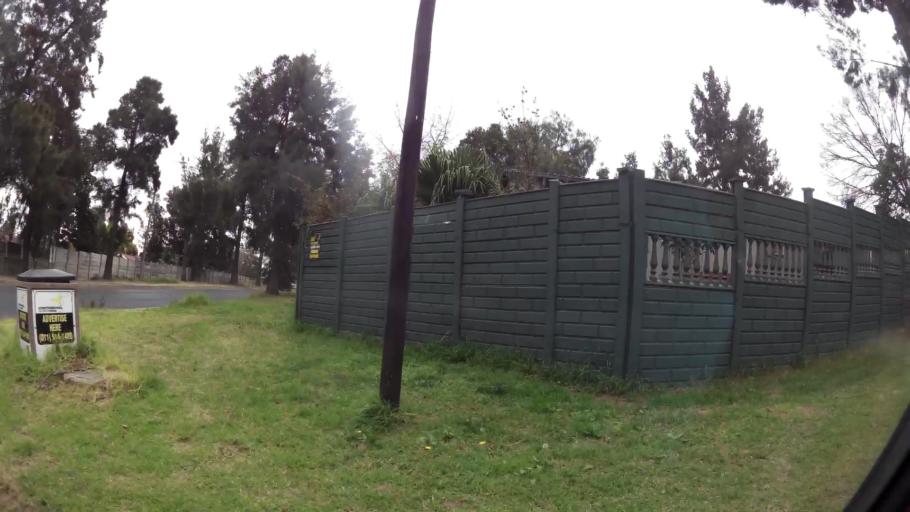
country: ZA
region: Gauteng
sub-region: City of Johannesburg Metropolitan Municipality
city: Roodepoort
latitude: -26.1136
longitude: 27.9055
